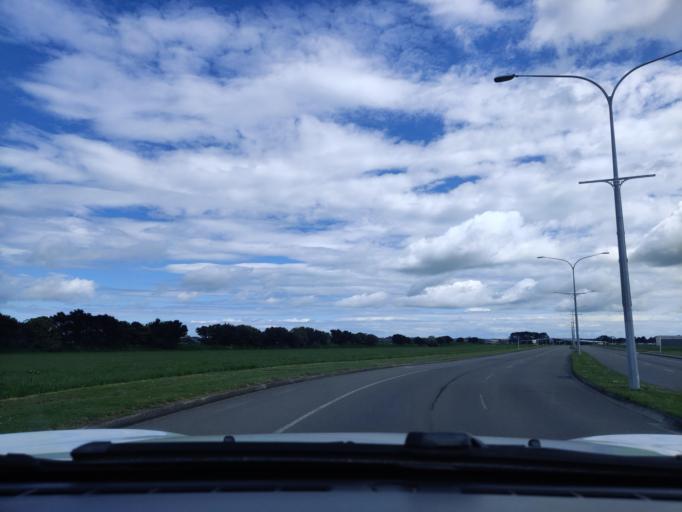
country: NZ
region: Manawatu-Wanganui
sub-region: Palmerston North City
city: Palmerston North
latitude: -40.3268
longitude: 175.6176
